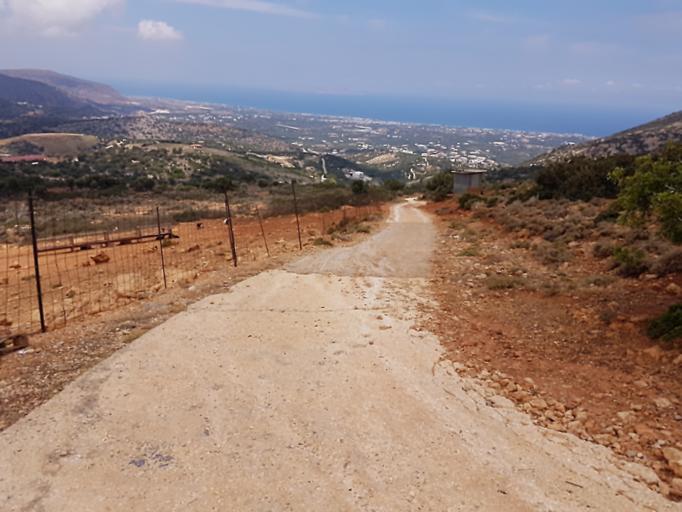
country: GR
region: Crete
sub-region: Nomos Irakleiou
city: Limin Khersonisou
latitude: 35.2918
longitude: 25.3773
